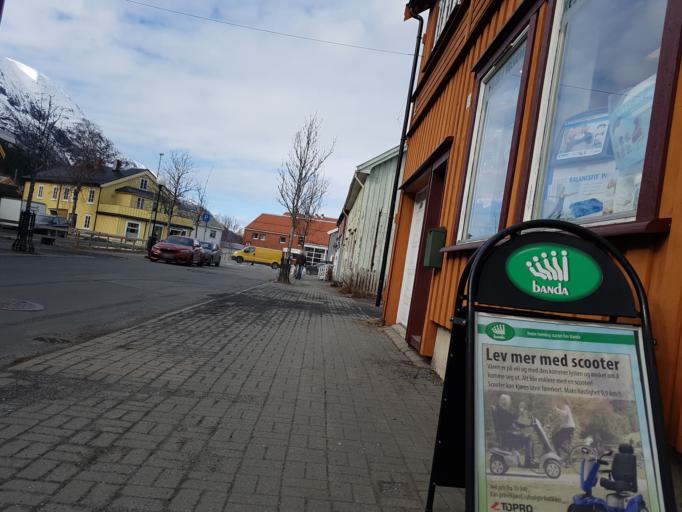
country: NO
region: Nordland
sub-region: Vefsn
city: Mosjoen
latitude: 65.8389
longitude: 13.1900
